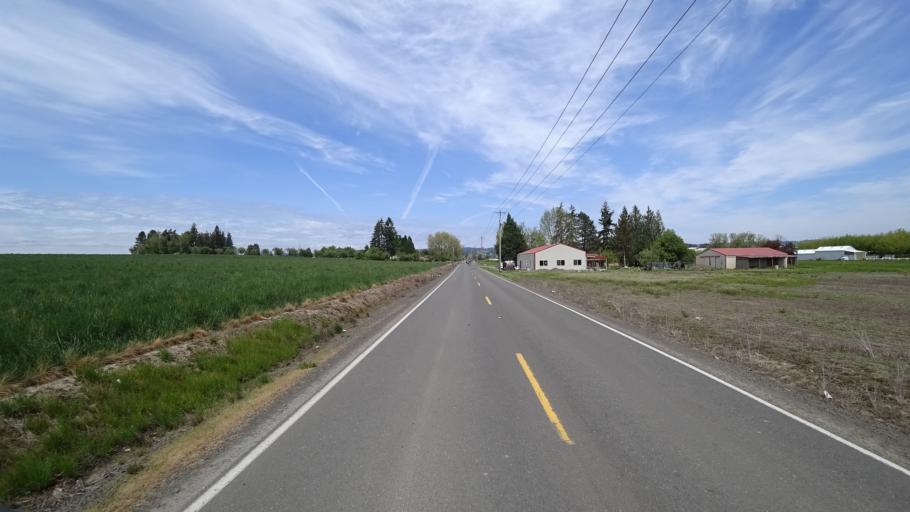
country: US
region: Oregon
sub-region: Washington County
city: Rockcreek
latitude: 45.5716
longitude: -122.9237
